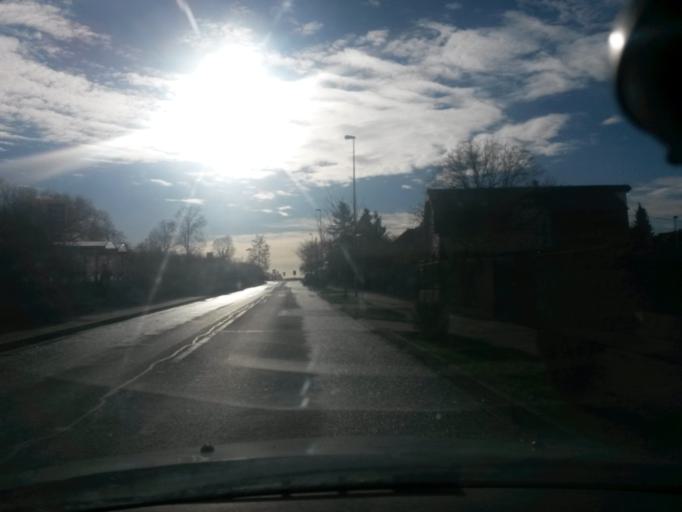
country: CZ
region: Central Bohemia
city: Vestec
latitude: 49.9961
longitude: 14.5181
